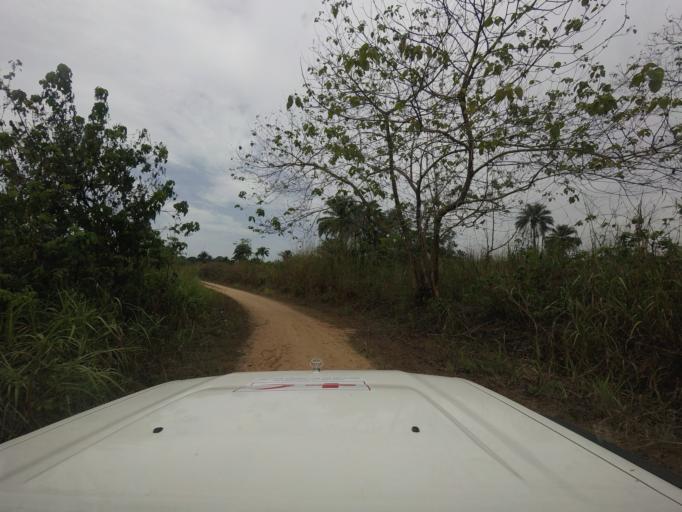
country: SL
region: Eastern Province
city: Buedu
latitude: 8.2682
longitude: -10.2859
